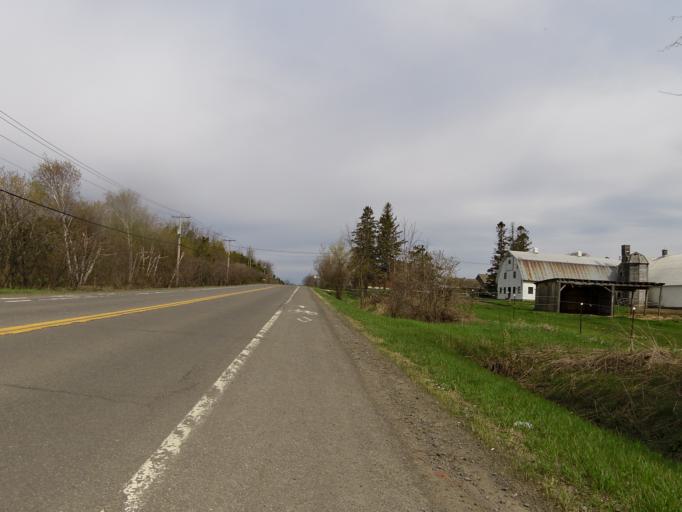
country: CA
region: Quebec
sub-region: Laurentides
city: Oka
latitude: 45.4698
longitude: -74.1190
